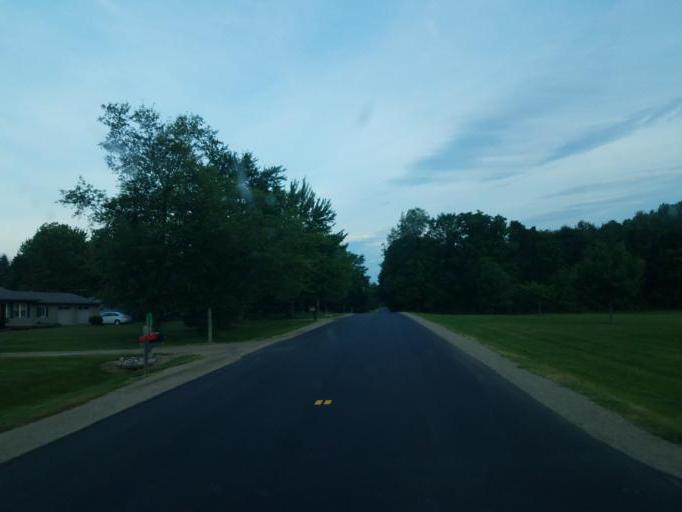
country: US
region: Michigan
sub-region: Eaton County
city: Charlotte
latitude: 42.5971
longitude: -84.8595
